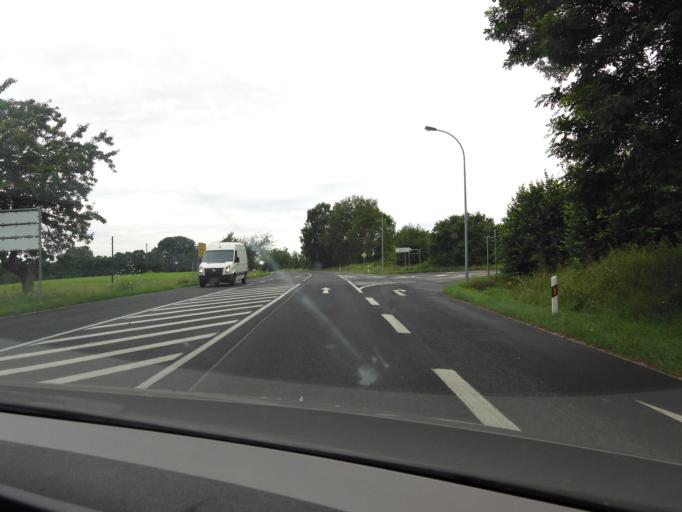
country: DE
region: Brandenburg
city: Lychen
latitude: 53.2097
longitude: 13.2760
